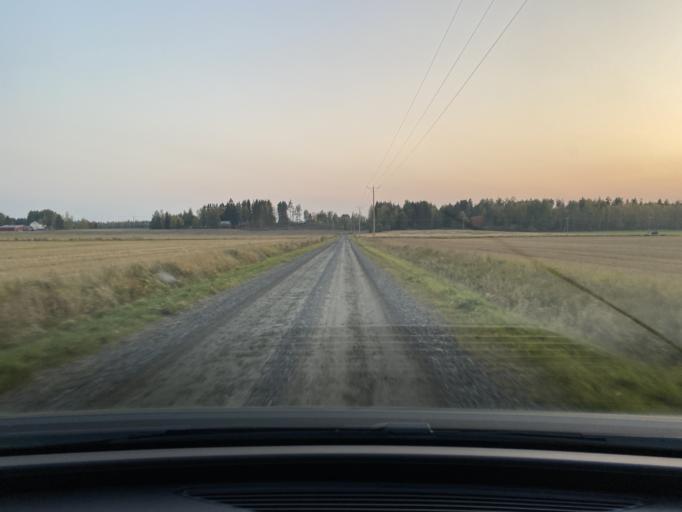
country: FI
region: Pirkanmaa
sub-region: Lounais-Pirkanmaa
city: Punkalaidun
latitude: 61.1037
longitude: 23.2136
